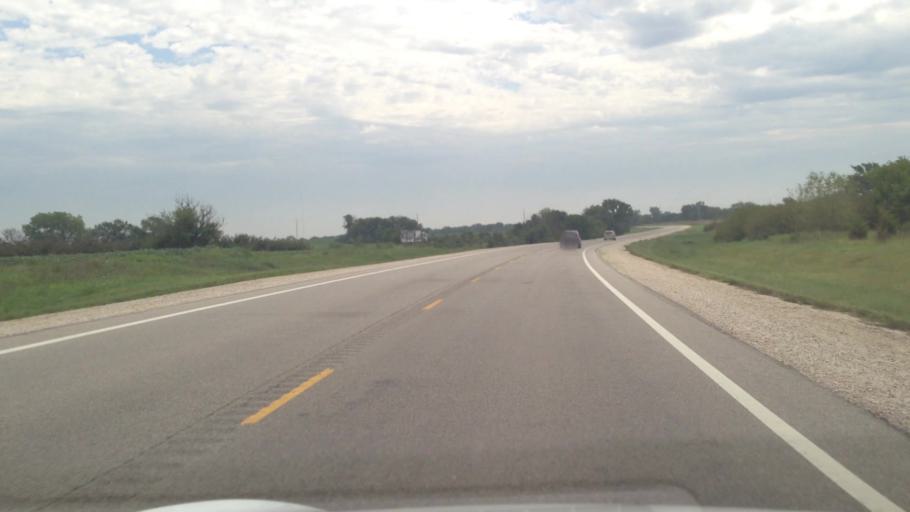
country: US
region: Kansas
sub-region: Allen County
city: Iola
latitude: 37.9200
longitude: -95.1577
